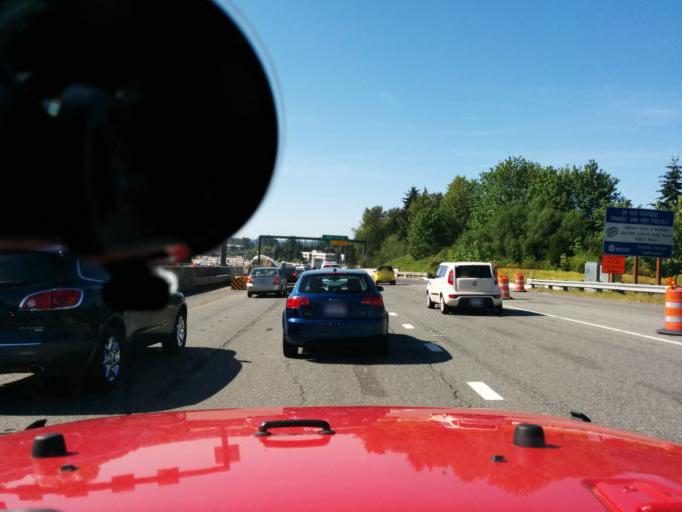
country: US
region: Washington
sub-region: King County
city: Clyde Hill
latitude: 47.6365
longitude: -122.1924
